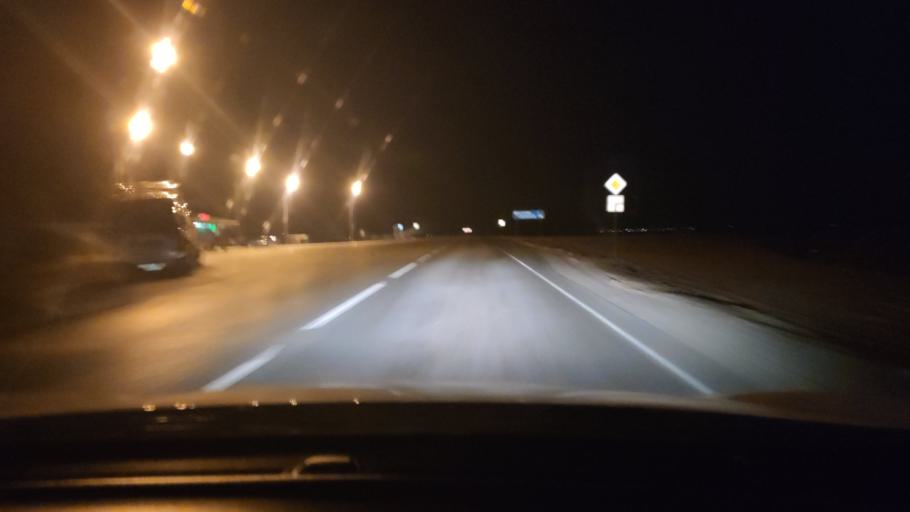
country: RU
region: Tatarstan
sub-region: Alekseyevskiy Rayon
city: Alekseyevskoye
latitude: 55.2904
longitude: 49.9703
